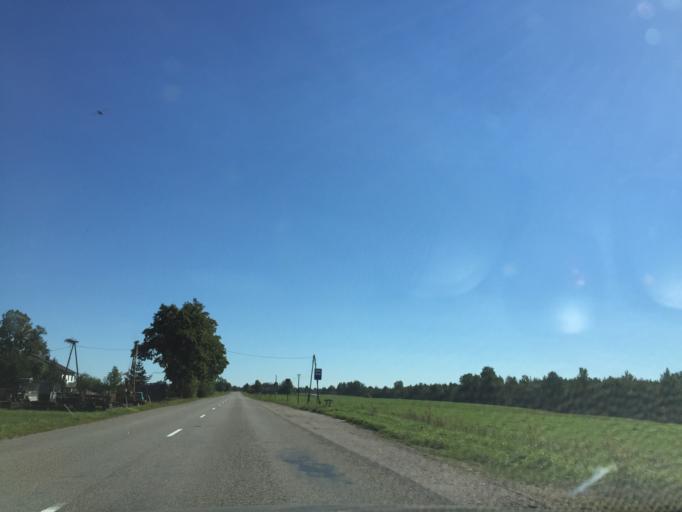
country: LV
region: Akniste
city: Akniste
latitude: 56.0656
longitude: 25.8940
